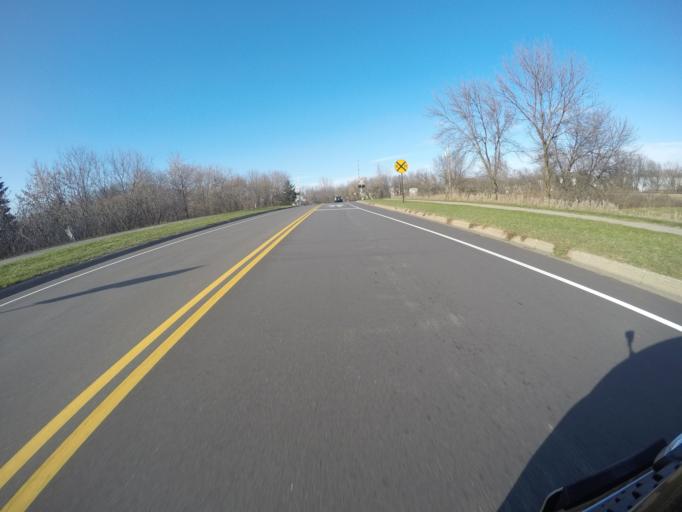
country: US
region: Minnesota
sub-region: Hennepin County
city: Eden Prairie
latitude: 44.8723
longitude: -93.4974
